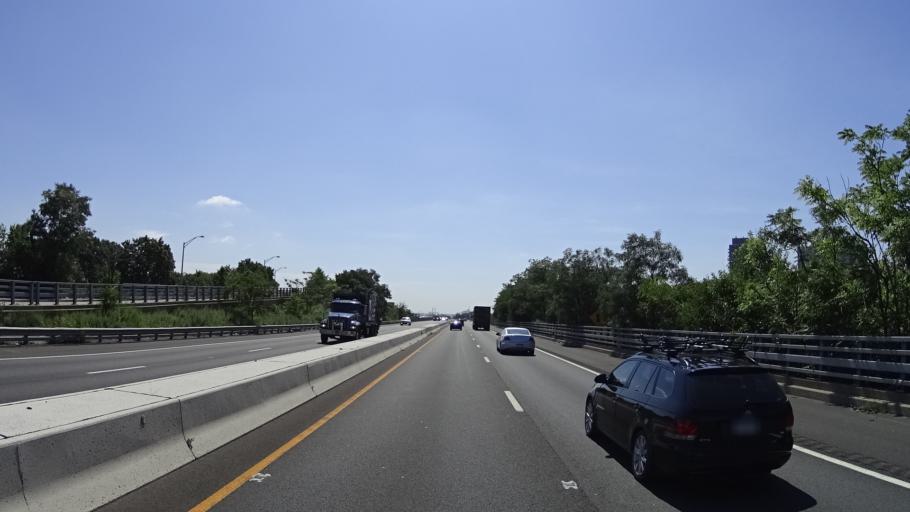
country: US
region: New Jersey
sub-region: Union County
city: Hillside
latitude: 40.7126
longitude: -74.2000
